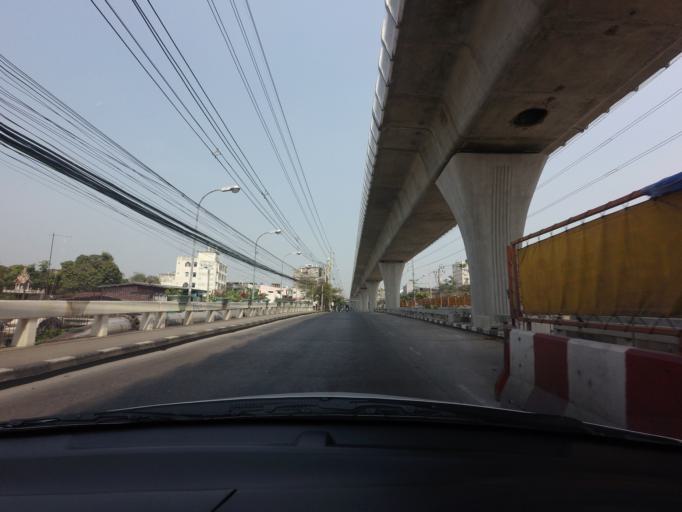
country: TH
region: Bangkok
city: Bangkok Yai
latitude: 13.7430
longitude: 100.4704
